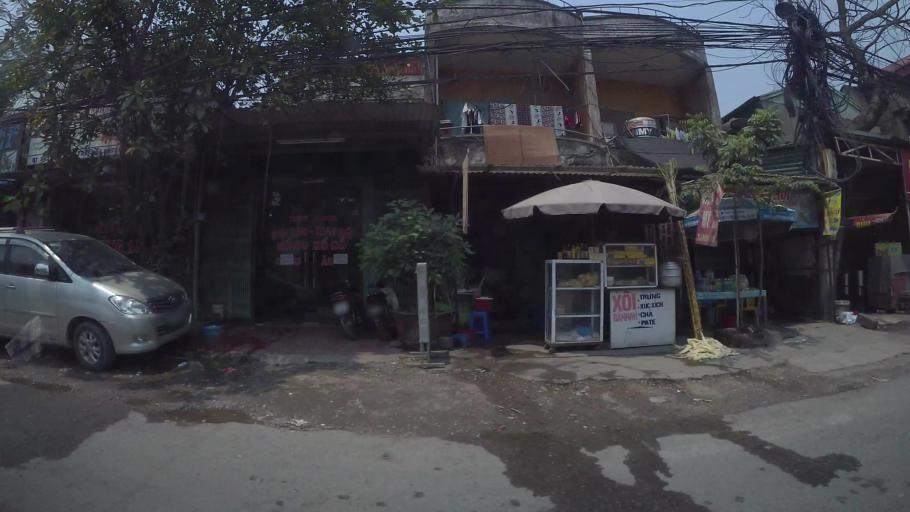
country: VN
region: Ha Noi
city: Van Dien
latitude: 20.9434
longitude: 105.8419
